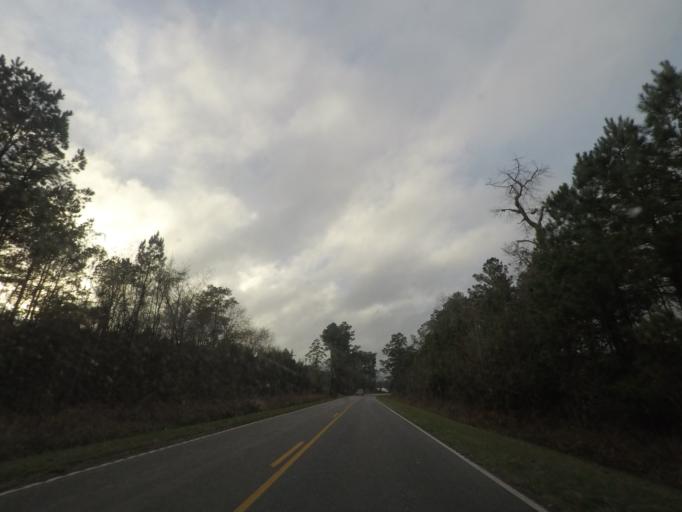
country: US
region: South Carolina
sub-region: Dorchester County
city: Saint George
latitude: 33.0501
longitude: -80.6087
